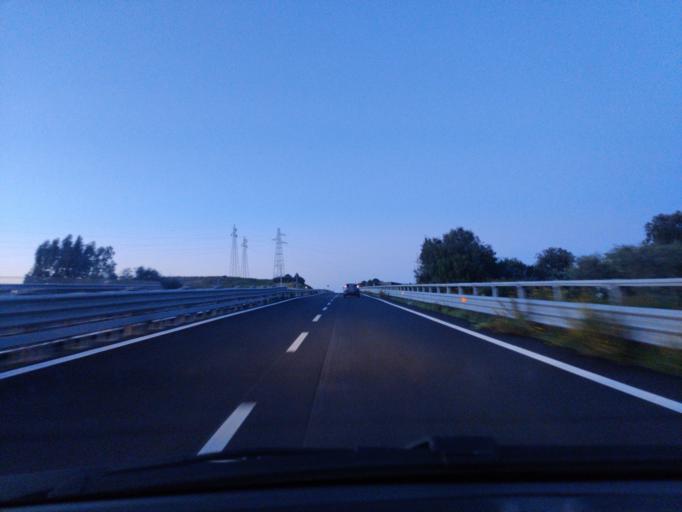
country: IT
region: Latium
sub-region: Citta metropolitana di Roma Capitale
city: Civitavecchia
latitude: 42.1101
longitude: 11.7927
